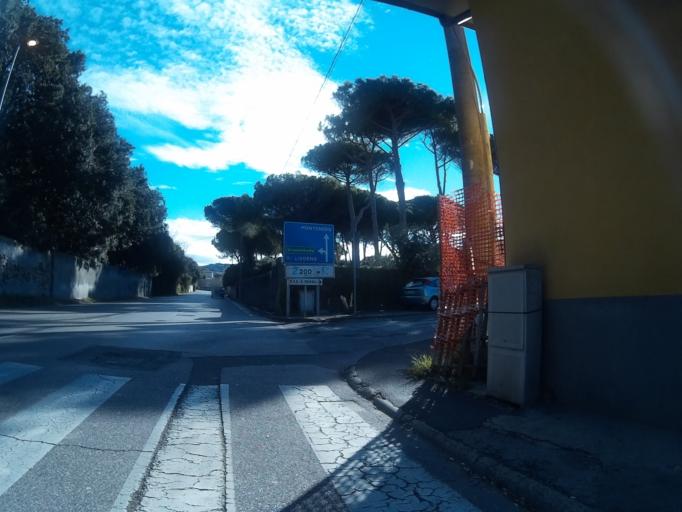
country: IT
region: Tuscany
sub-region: Provincia di Livorno
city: Livorno
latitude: 43.5110
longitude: 10.3298
